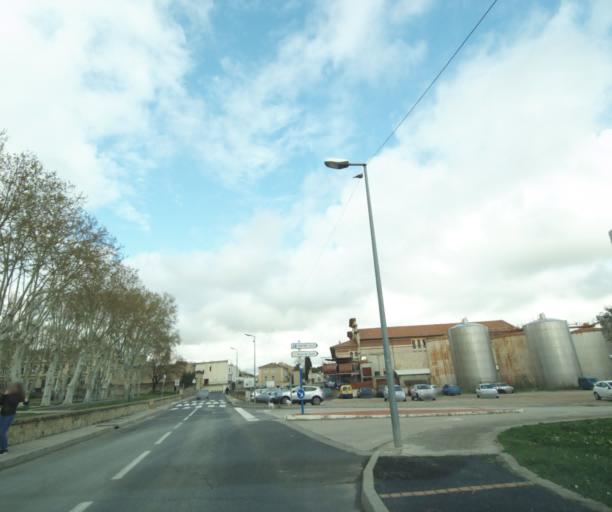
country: FR
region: Languedoc-Roussillon
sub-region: Departement de l'Herault
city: Pignan
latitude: 43.5802
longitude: 3.7612
